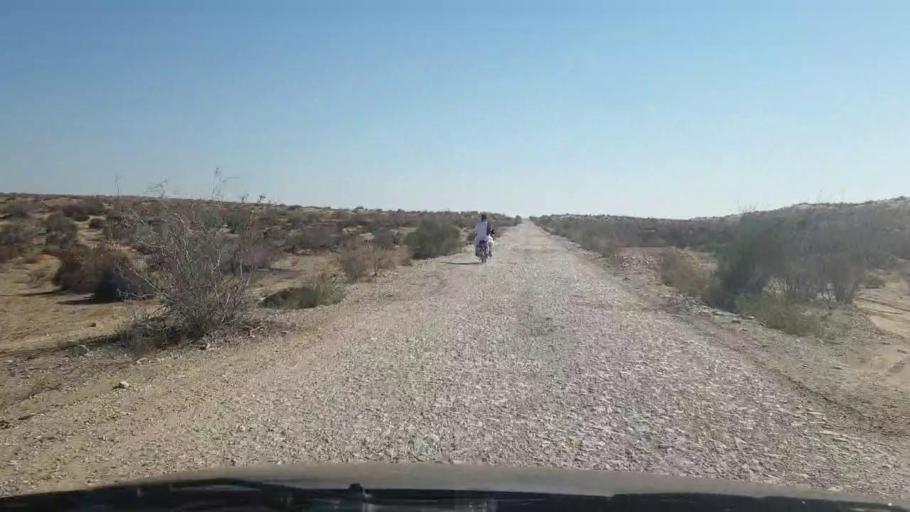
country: PK
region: Sindh
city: Bozdar
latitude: 27.0288
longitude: 68.7070
